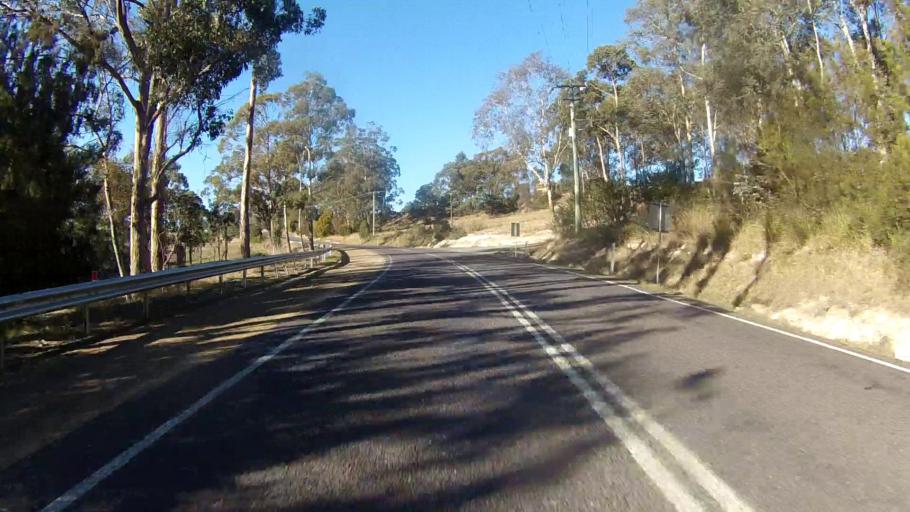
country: AU
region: Tasmania
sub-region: Sorell
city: Sorell
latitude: -42.8160
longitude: 147.6652
